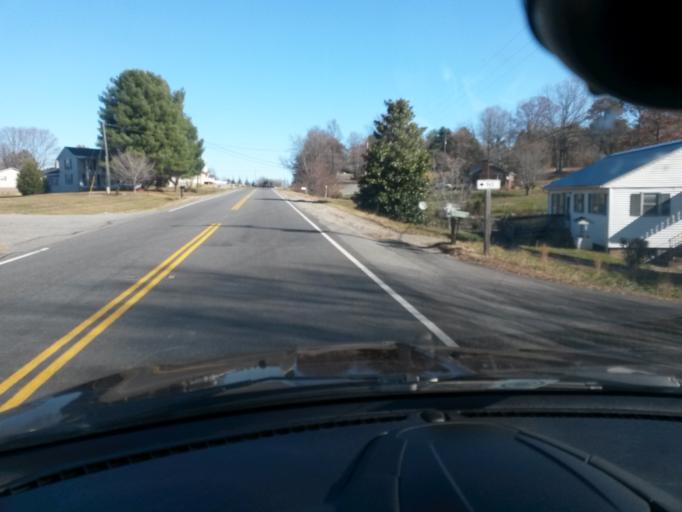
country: US
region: Virginia
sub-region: Henry County
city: Pannill Fork
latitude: 36.7534
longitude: -80.0649
